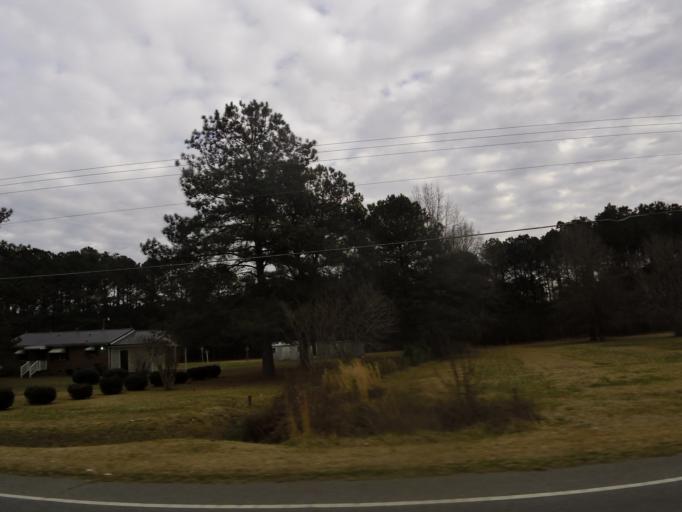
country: US
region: North Carolina
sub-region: Northampton County
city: Jackson
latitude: 36.3055
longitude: -77.2659
